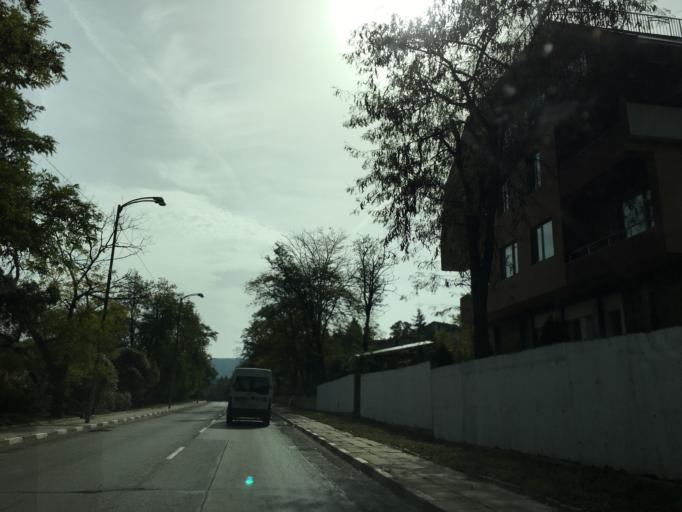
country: BG
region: Sofia-Capital
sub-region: Stolichna Obshtina
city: Sofia
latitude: 42.5891
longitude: 23.4192
